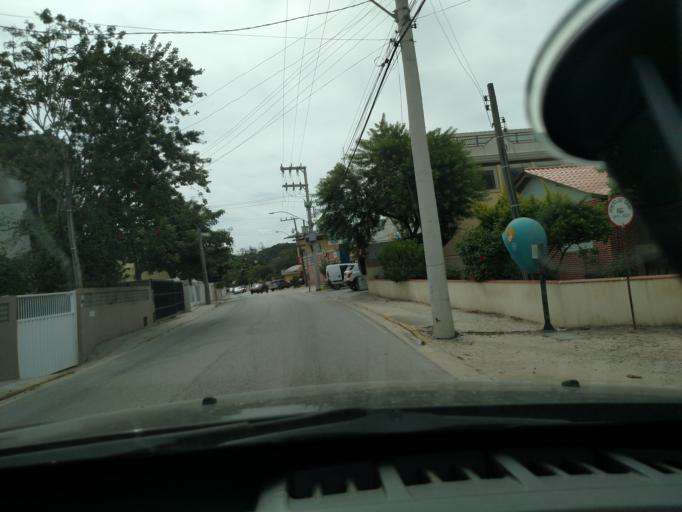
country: BR
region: Santa Catarina
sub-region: Porto Belo
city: Porto Belo
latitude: -27.1849
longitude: -48.5123
